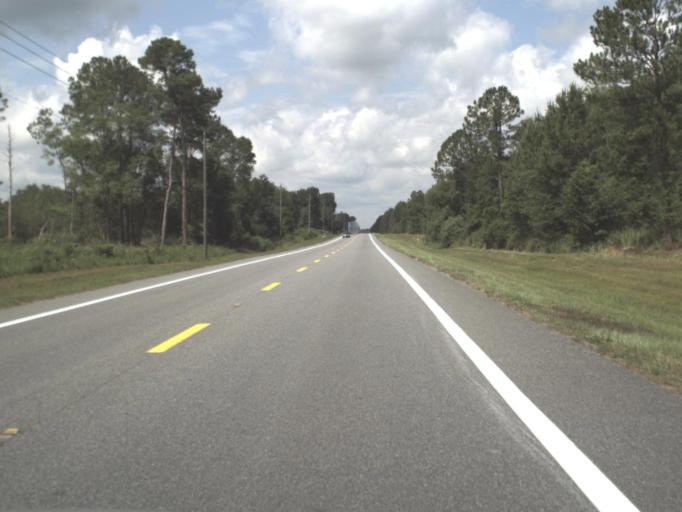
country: US
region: Florida
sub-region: Union County
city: Lake Butler
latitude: 30.0566
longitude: -82.2514
